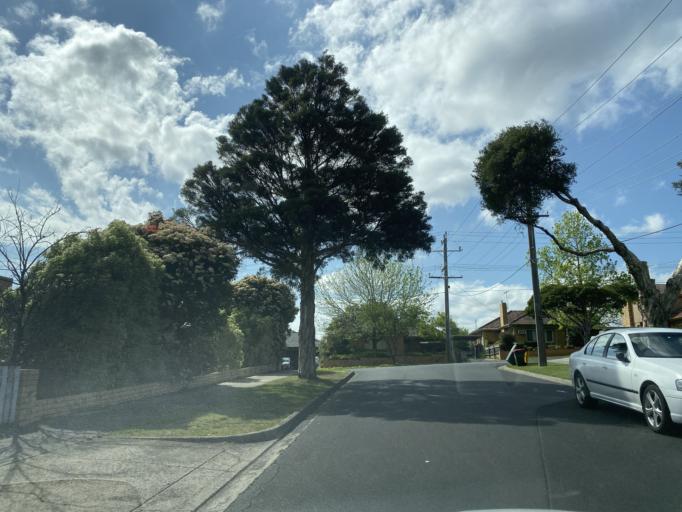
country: AU
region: Victoria
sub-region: Whitehorse
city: Burwood
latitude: -37.8488
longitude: 145.1277
